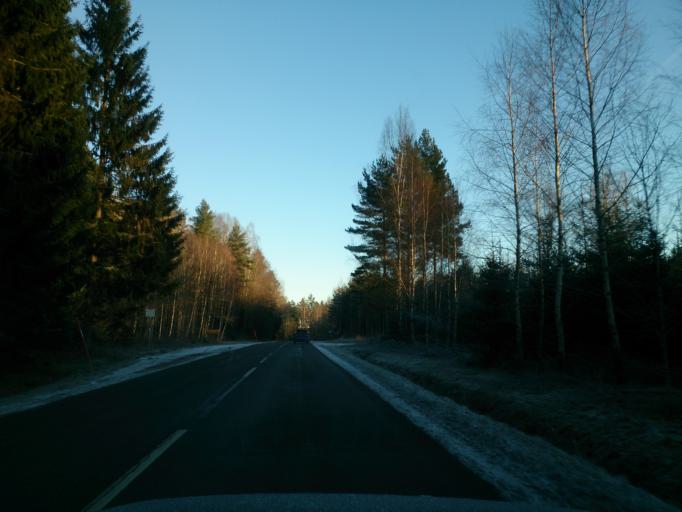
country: SE
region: OEstergoetland
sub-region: Norrkopings Kommun
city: Kimstad
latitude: 58.3742
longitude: 16.0260
